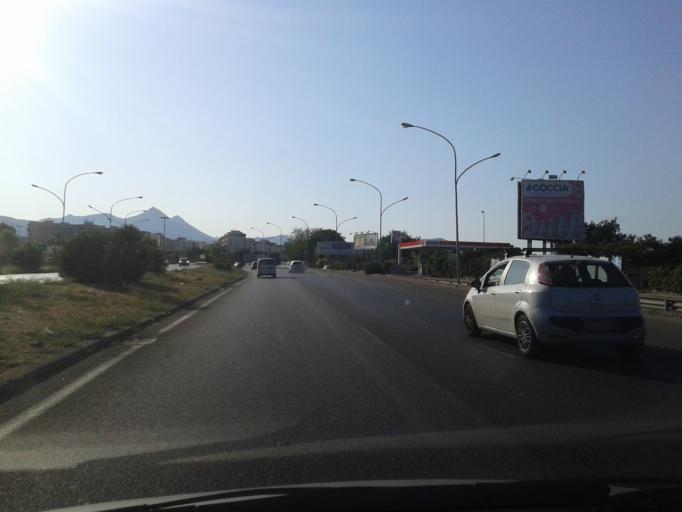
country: IT
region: Sicily
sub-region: Palermo
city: Ciaculli
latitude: 38.0903
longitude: 13.3829
